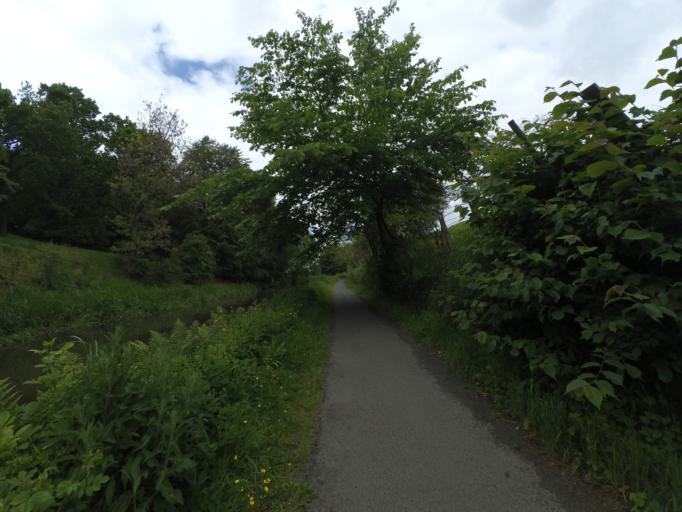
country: GB
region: Scotland
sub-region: Falkirk
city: Polmont
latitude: 55.9795
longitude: -3.6870
